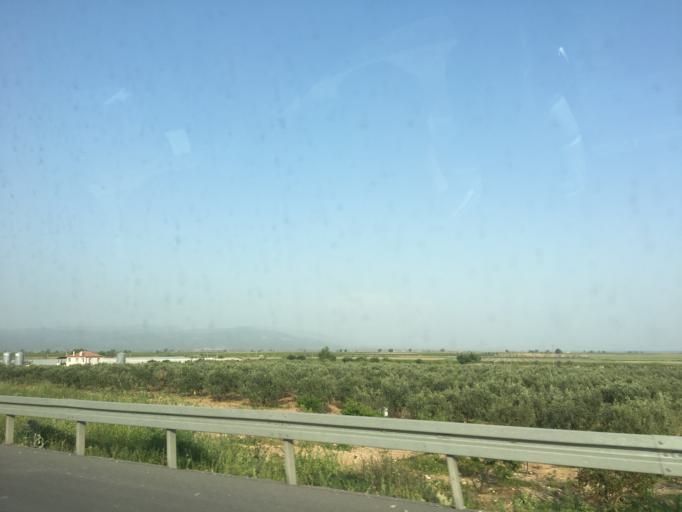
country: TR
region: Manisa
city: Golmarmara
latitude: 38.6587
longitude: 27.9412
